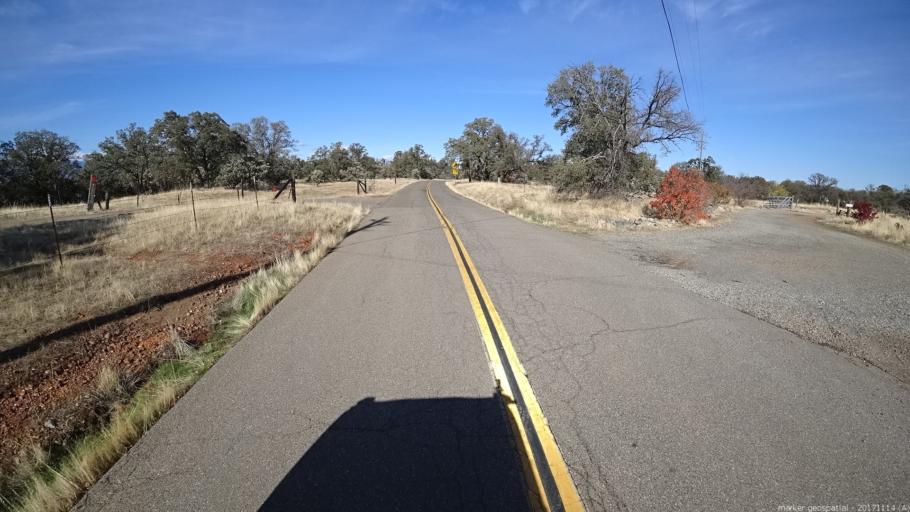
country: US
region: California
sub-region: Shasta County
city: Anderson
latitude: 40.4075
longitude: -122.4106
